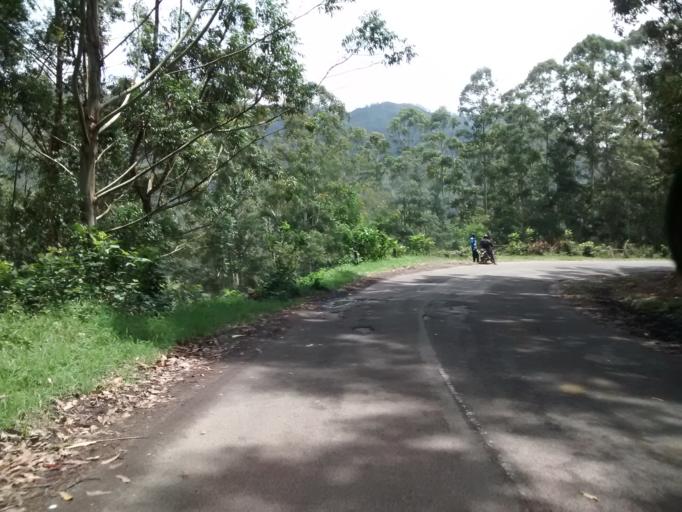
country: IN
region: Kerala
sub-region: Idukki
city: Munnar
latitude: 10.1130
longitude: 77.1333
